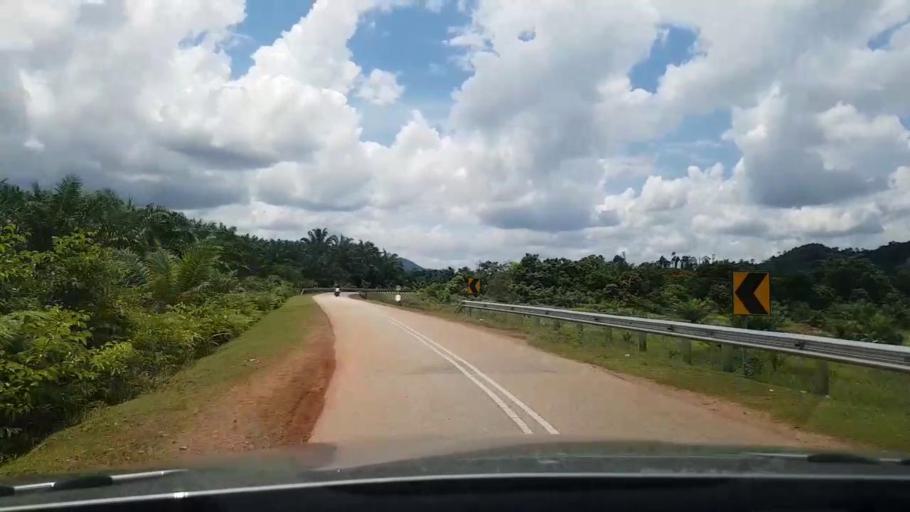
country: MY
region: Pahang
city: Pekan
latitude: 3.1080
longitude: 102.9786
